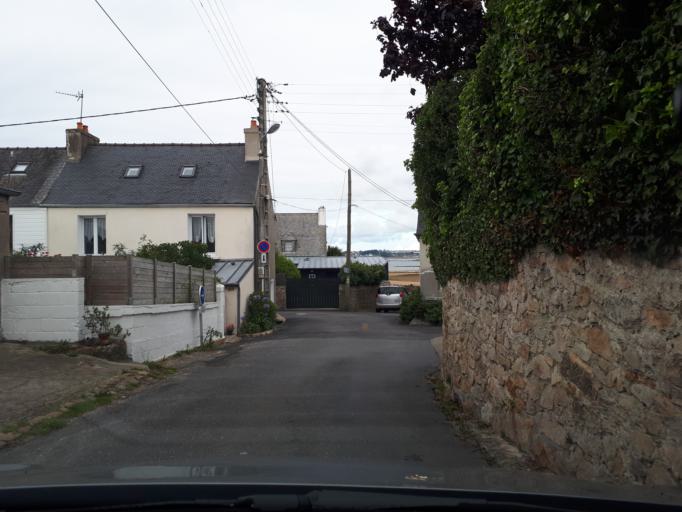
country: FR
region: Brittany
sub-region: Departement du Finistere
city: Carantec
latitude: 48.6743
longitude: -3.9226
